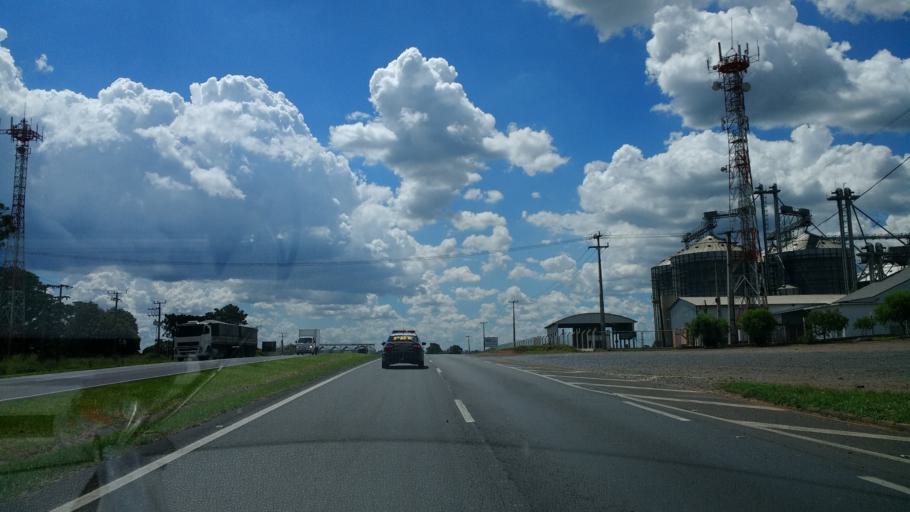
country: BR
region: Parana
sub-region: Ponta Grossa
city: Ponta Grossa
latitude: -25.2209
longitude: -50.0534
